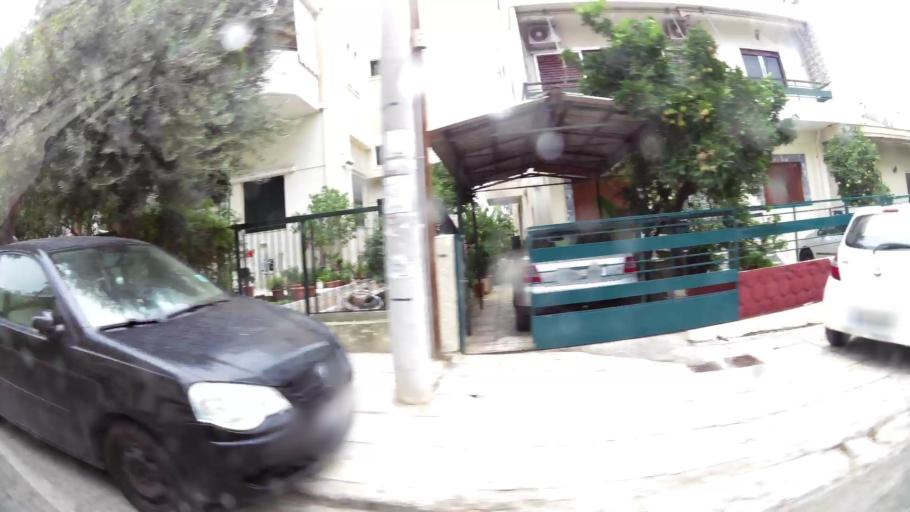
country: GR
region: Attica
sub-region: Nomarchia Athinas
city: Palaio Faliro
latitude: 37.9306
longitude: 23.6990
